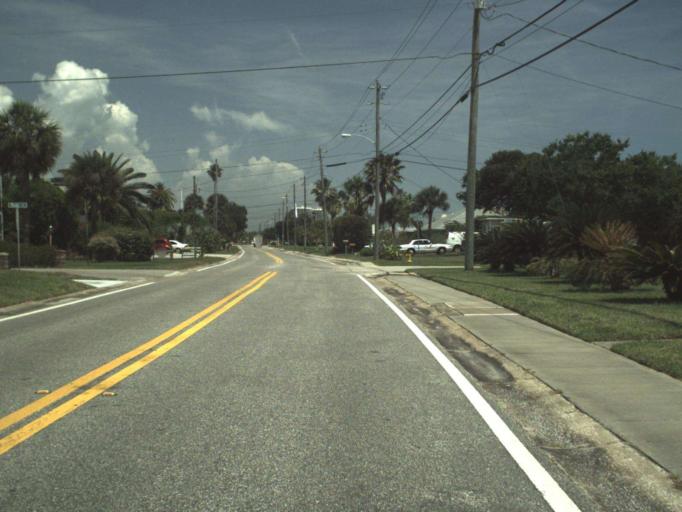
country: US
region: Florida
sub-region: Volusia County
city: Daytona Beach Shores
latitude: 29.1528
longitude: -80.9728
